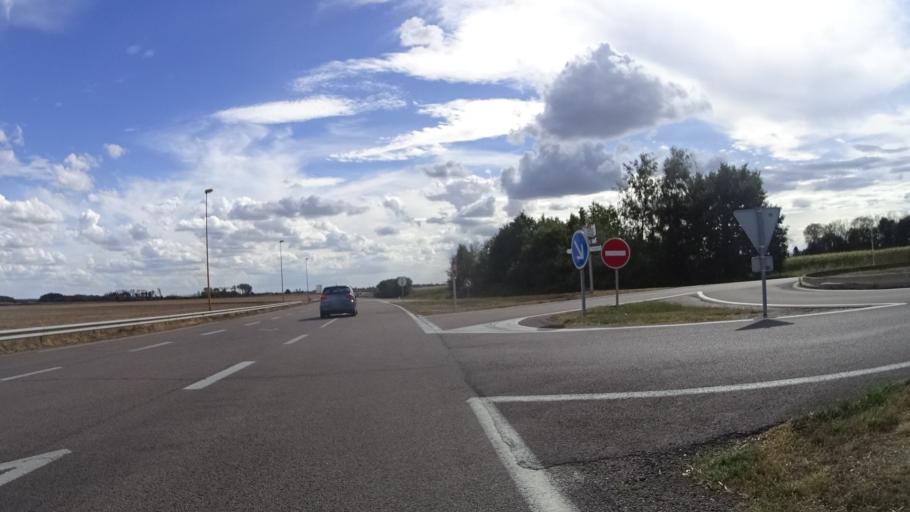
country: FR
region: Bourgogne
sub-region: Departement de la Cote-d'Or
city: Seurre
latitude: 47.0276
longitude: 5.1710
